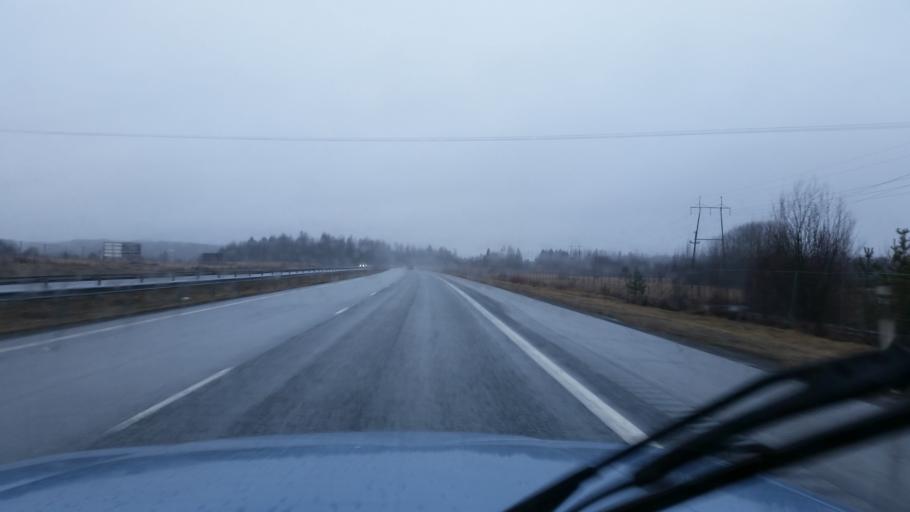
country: FI
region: Pirkanmaa
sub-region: Etelae-Pirkanmaa
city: Akaa
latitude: 61.1926
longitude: 23.8641
